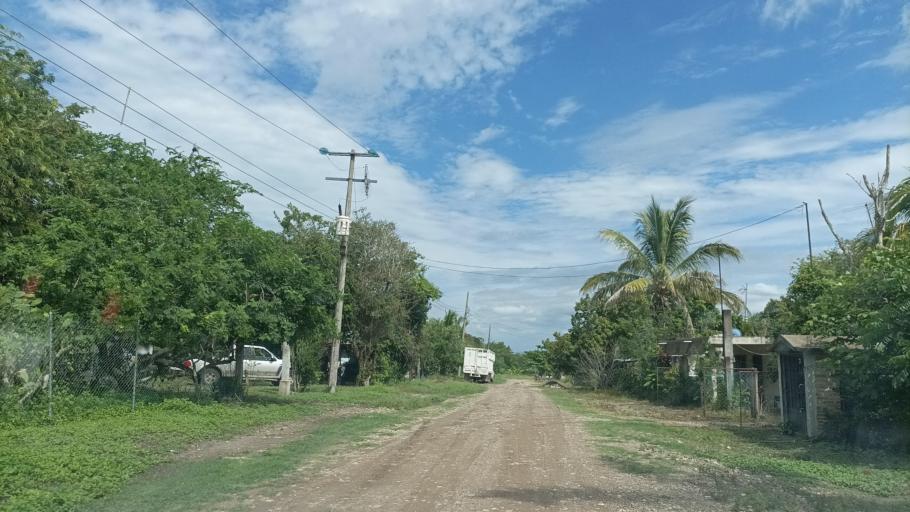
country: MX
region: Veracruz
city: Panuco
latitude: 21.9461
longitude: -98.1368
